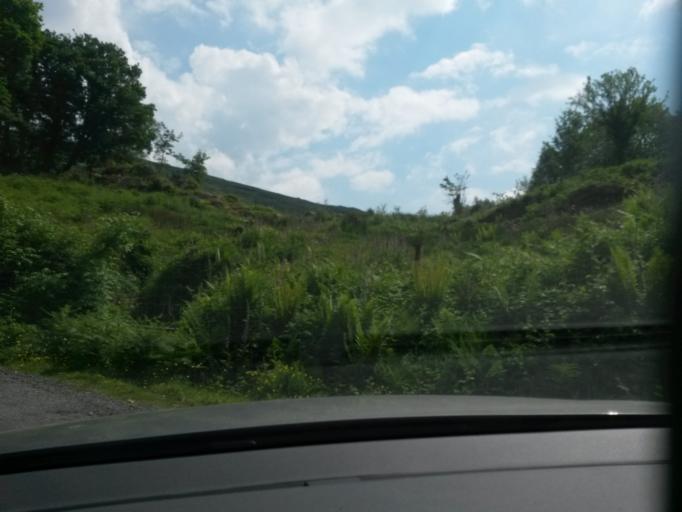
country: IE
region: Munster
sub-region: Ciarrai
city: Kenmare
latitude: 51.8110
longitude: -9.5362
